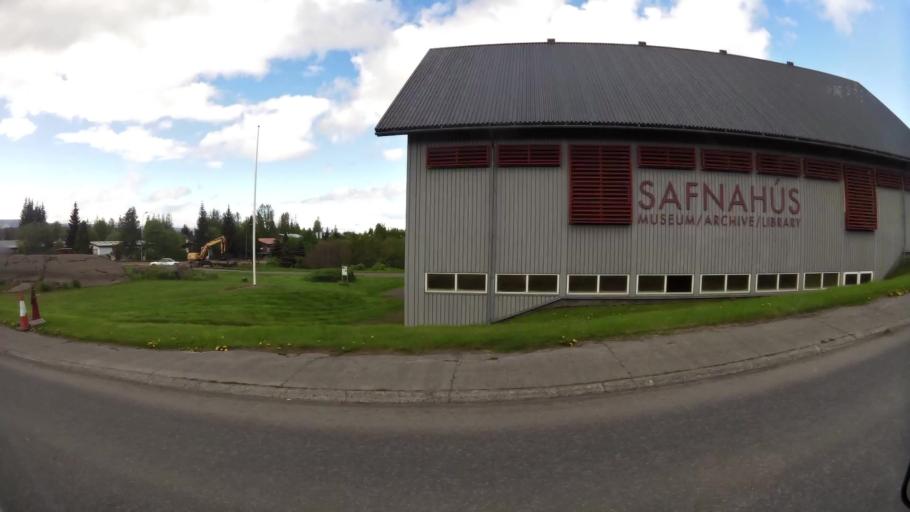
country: IS
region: East
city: Egilsstadir
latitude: 65.2625
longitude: -14.3971
